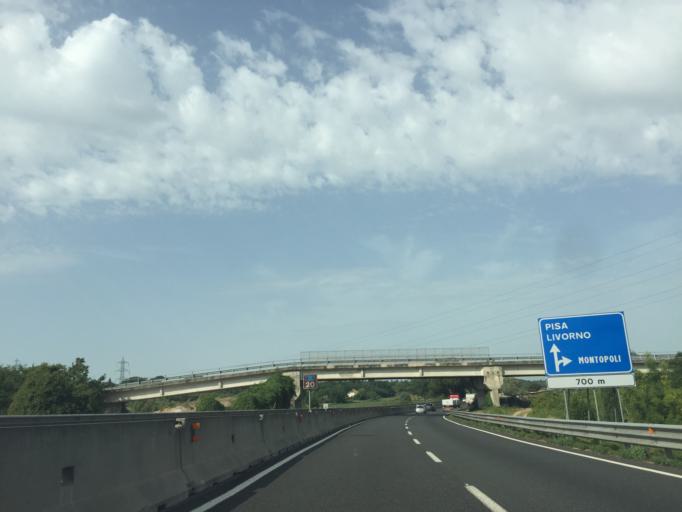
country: IT
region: Tuscany
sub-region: Province of Pisa
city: Montopoli
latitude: 43.6722
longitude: 10.7411
